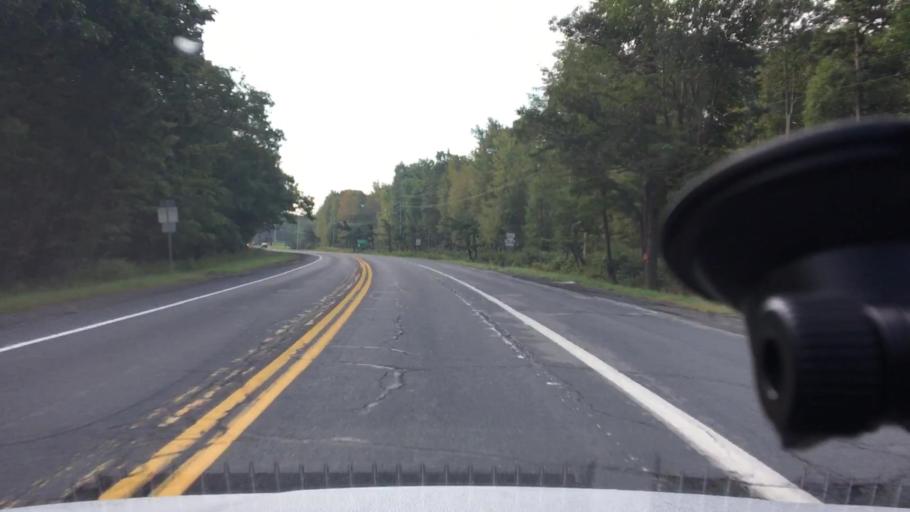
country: US
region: Pennsylvania
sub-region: Monroe County
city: Mount Pocono
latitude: 41.1091
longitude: -75.3856
